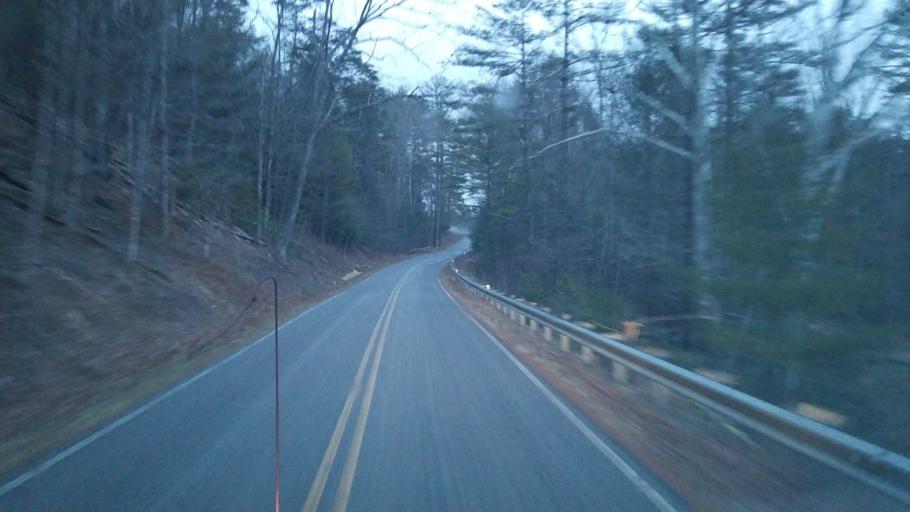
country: US
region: Virginia
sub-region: Pulaski County
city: Pulaski
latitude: 37.1102
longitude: -80.8891
